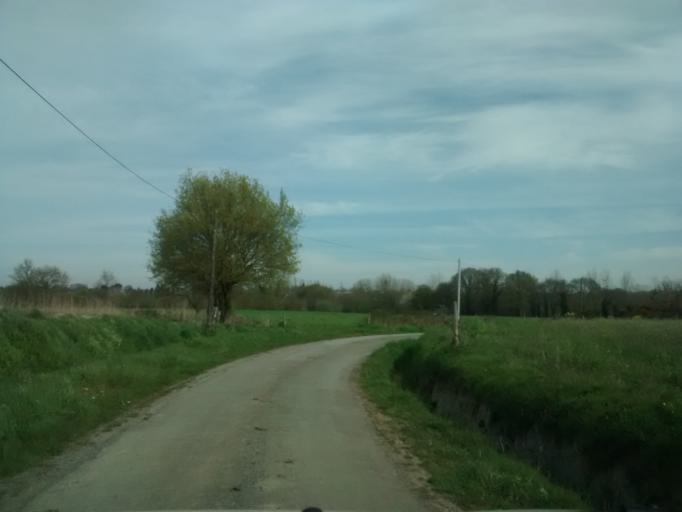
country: FR
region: Brittany
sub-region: Departement d'Ille-et-Vilaine
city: Noyal-sur-Vilaine
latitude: 48.1251
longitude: -1.5246
